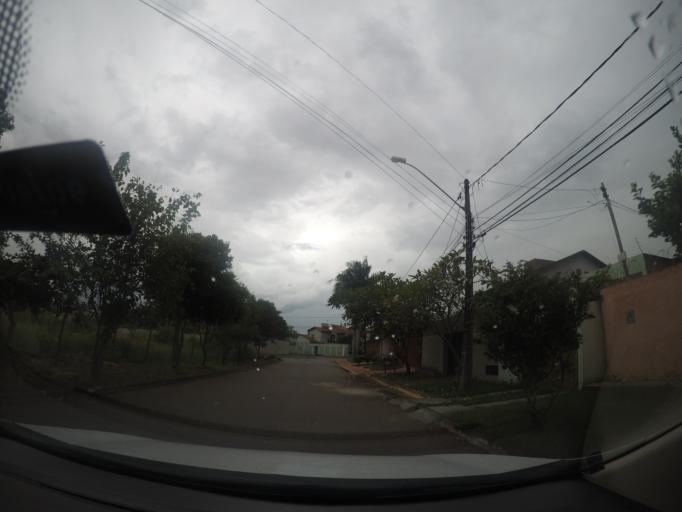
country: BR
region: Goias
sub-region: Goiania
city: Goiania
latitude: -16.6429
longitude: -49.2341
